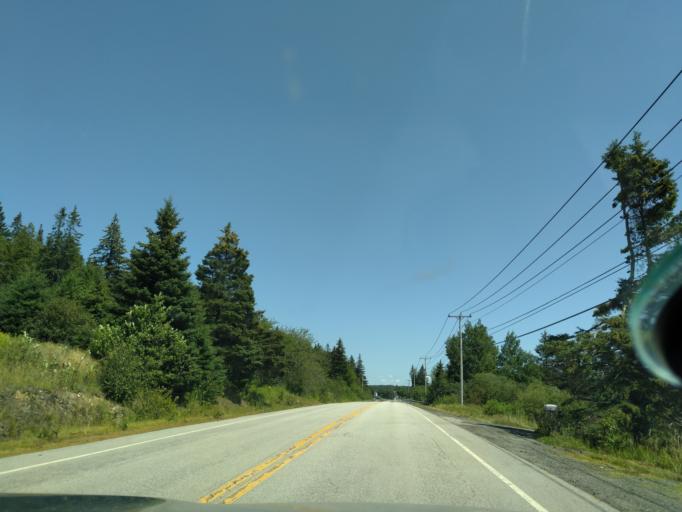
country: US
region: Maine
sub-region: Washington County
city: Eastport
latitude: 44.8100
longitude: -67.0849
